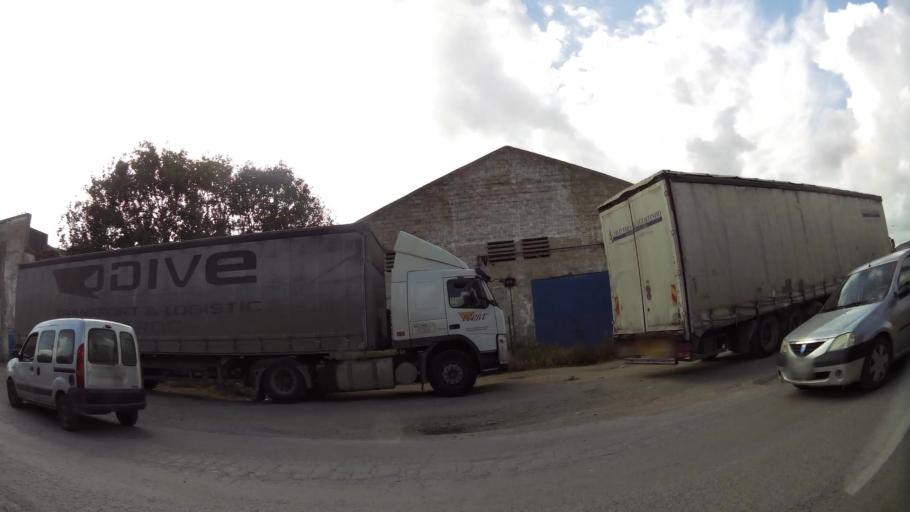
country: MA
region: Gharb-Chrarda-Beni Hssen
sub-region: Kenitra Province
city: Kenitra
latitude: 34.2758
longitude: -6.5610
